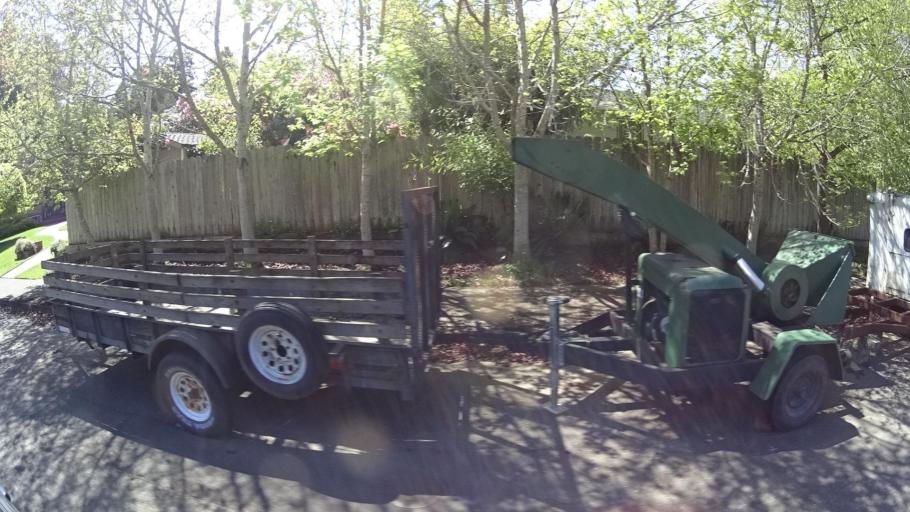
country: US
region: California
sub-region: Humboldt County
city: Cutten
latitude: 40.7827
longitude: -124.1477
